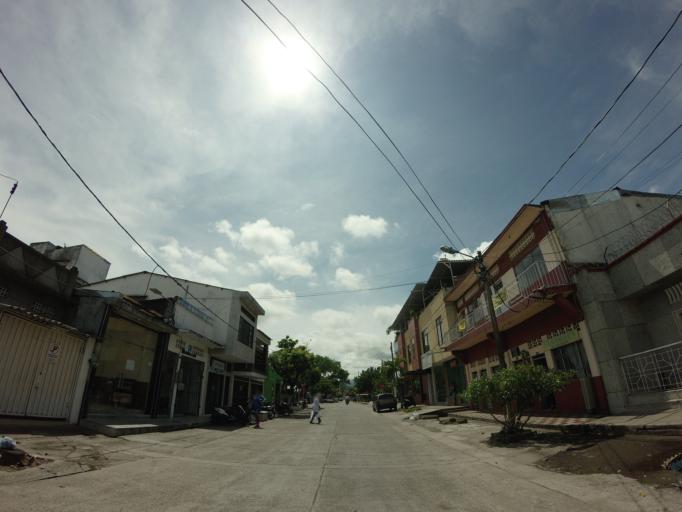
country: CO
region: Caldas
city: La Dorada
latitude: 5.4516
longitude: -74.6650
